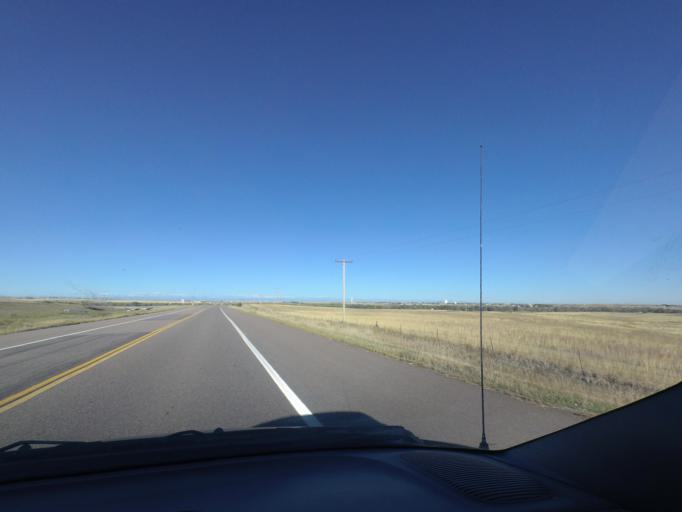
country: US
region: Colorado
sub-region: Adams County
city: Bennett
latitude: 39.7382
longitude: -104.4018
